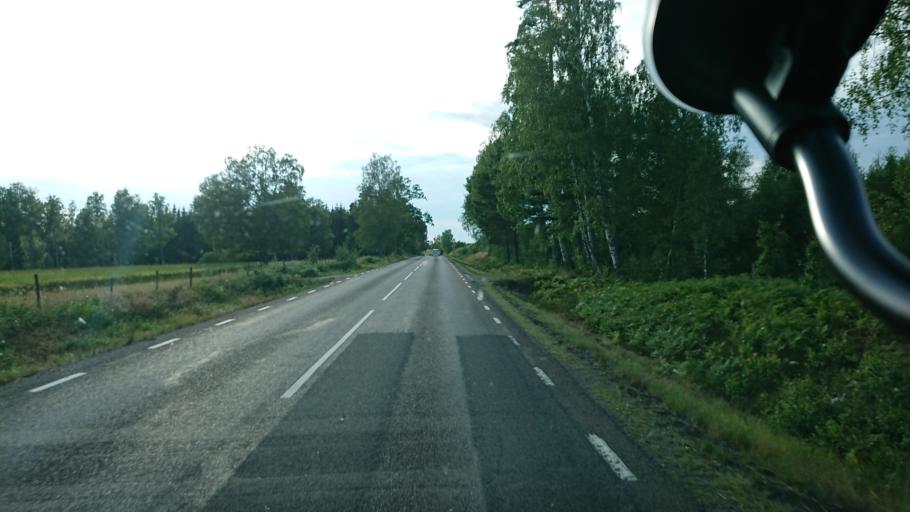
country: SE
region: Kronoberg
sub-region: Vaxjo Kommun
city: Braas
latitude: 57.0186
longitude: 15.0450
